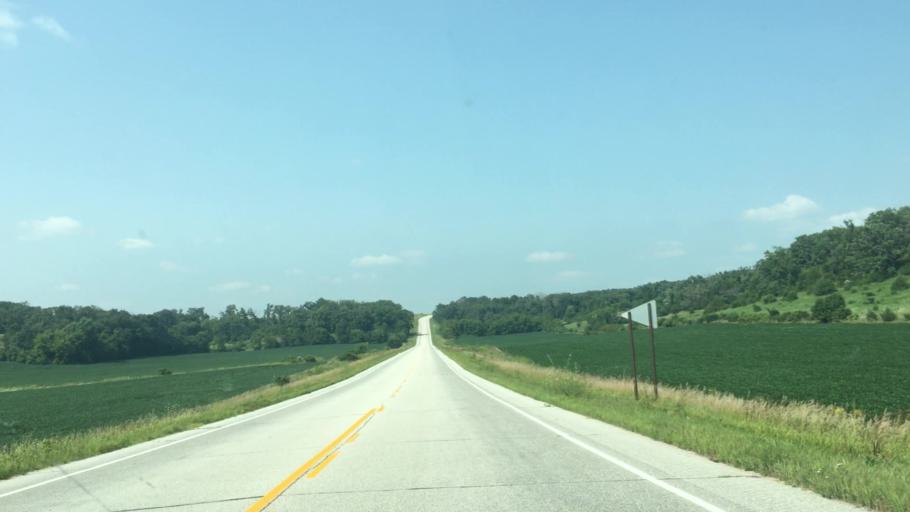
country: US
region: Minnesota
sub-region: Fillmore County
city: Harmony
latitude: 43.6319
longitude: -91.9299
